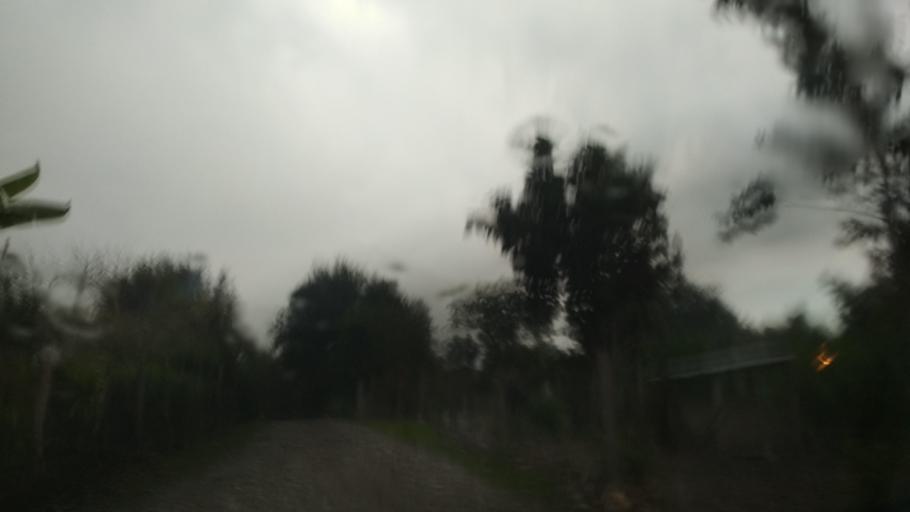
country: MM
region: Shan
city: Taunggyi
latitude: 20.3048
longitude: 97.3055
